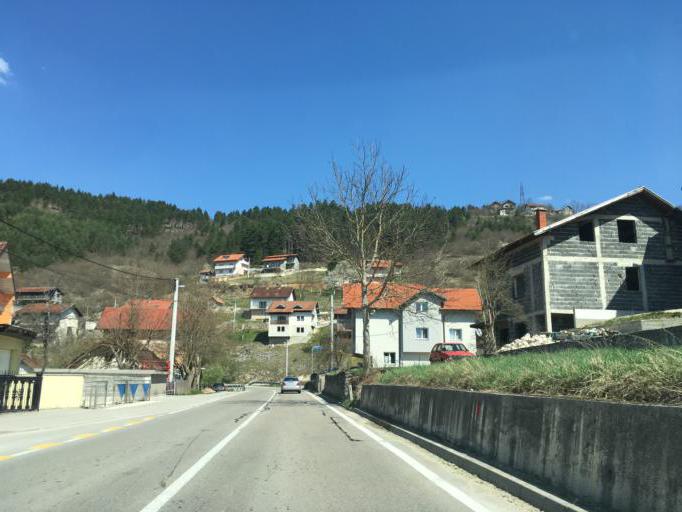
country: BA
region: Federation of Bosnia and Herzegovina
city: Divicani
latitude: 44.3684
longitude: 17.3000
